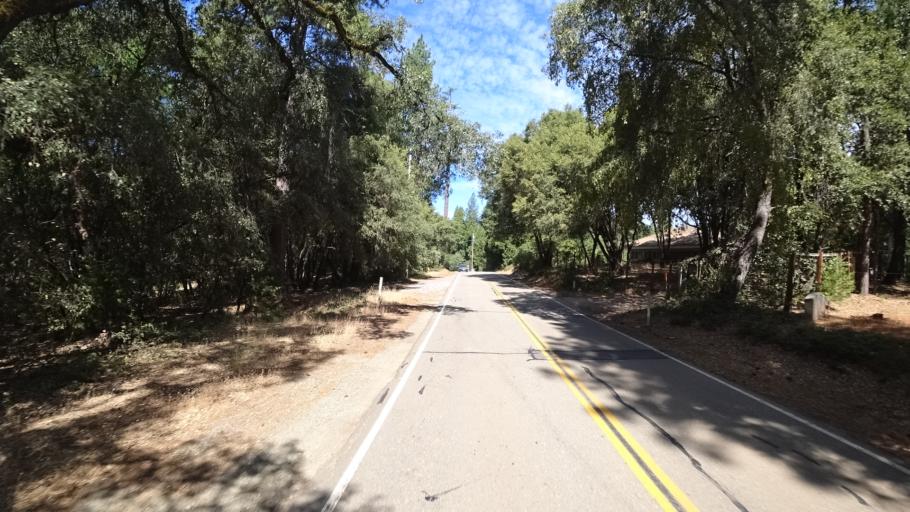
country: US
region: California
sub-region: Amador County
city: Pioneer
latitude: 38.3387
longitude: -120.5455
